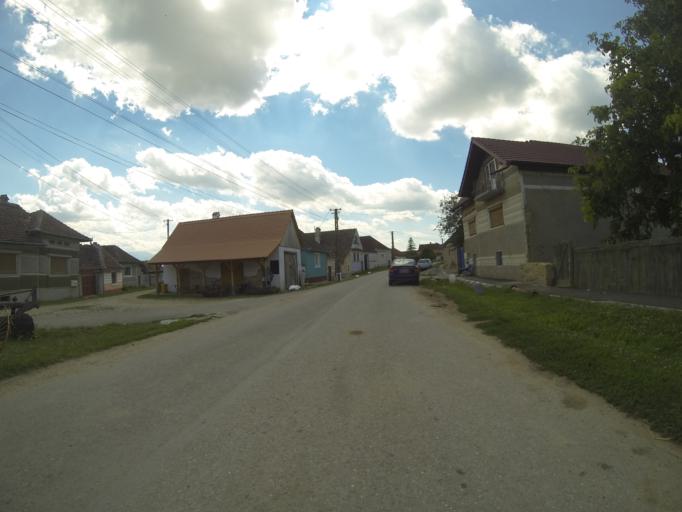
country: RO
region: Brasov
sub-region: Comuna Mandra
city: Mandra
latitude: 45.8465
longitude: 25.0395
